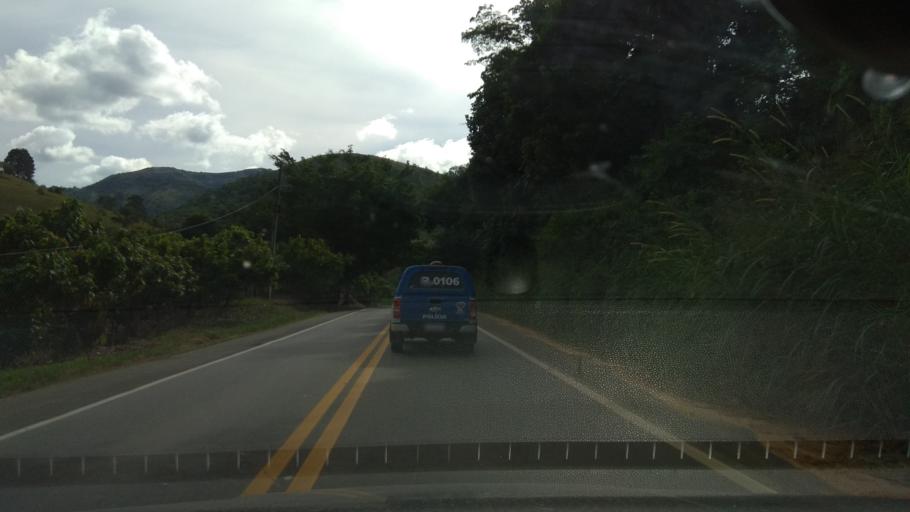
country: BR
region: Bahia
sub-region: Jitauna
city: Jitauna
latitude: -14.0060
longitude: -39.9214
